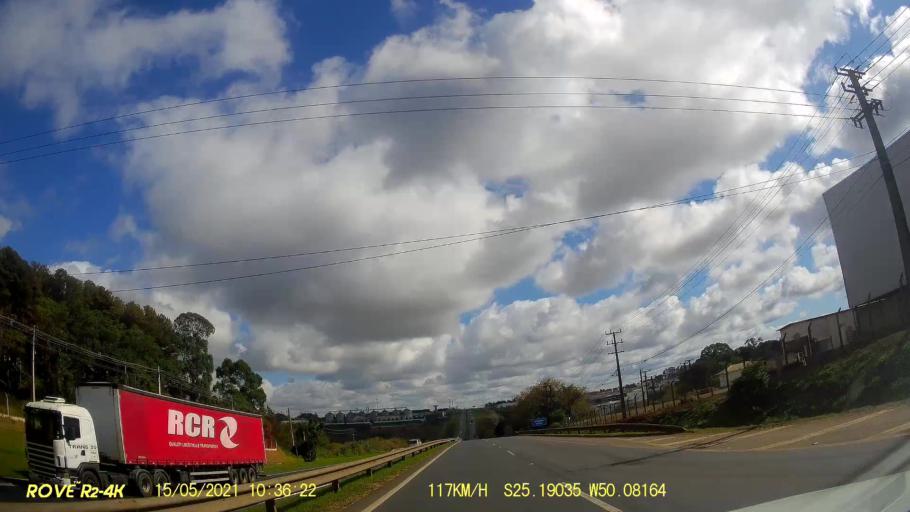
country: BR
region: Parana
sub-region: Ponta Grossa
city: Ponta Grossa
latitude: -25.1905
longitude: -50.0822
